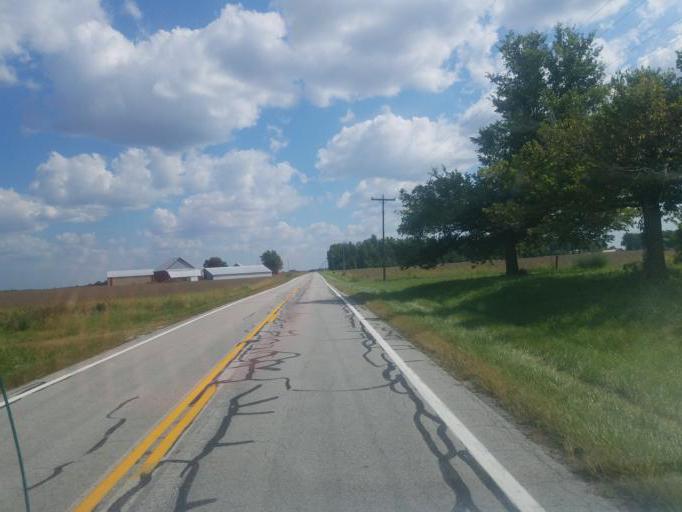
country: US
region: Ohio
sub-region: Allen County
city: Spencerville
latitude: 40.6570
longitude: -84.3453
